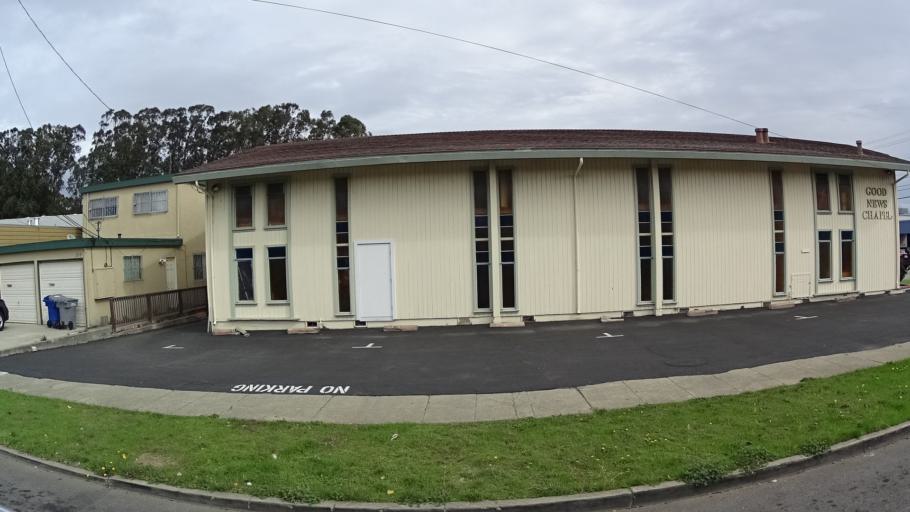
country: US
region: California
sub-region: San Mateo County
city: South San Francisco
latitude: 37.6515
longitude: -122.4282
